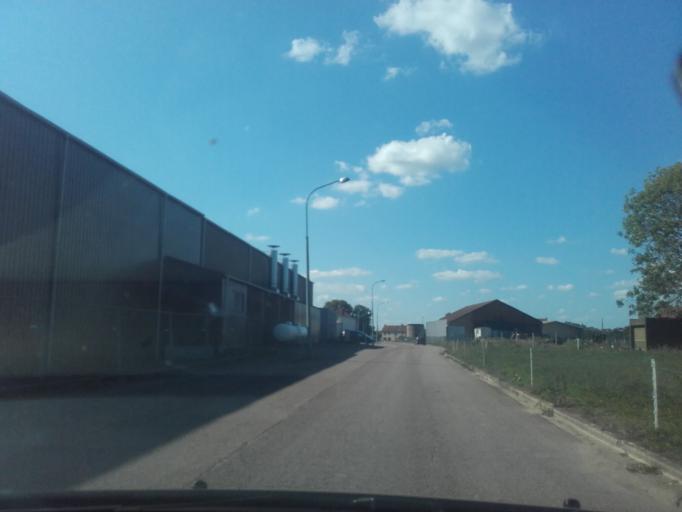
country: FR
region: Bourgogne
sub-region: Departement de Saone-et-Loire
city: Epinac
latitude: 46.9840
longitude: 4.5223
